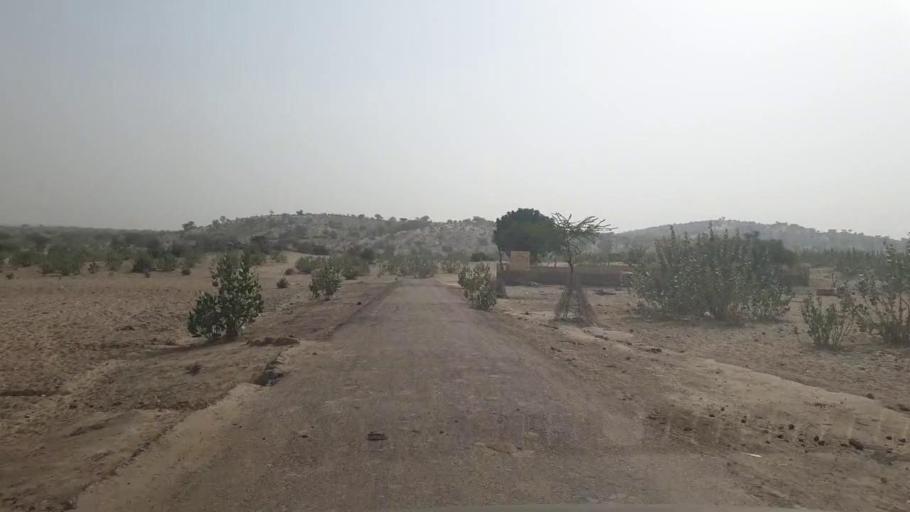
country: PK
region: Sindh
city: Chor
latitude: 25.6202
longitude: 69.9234
